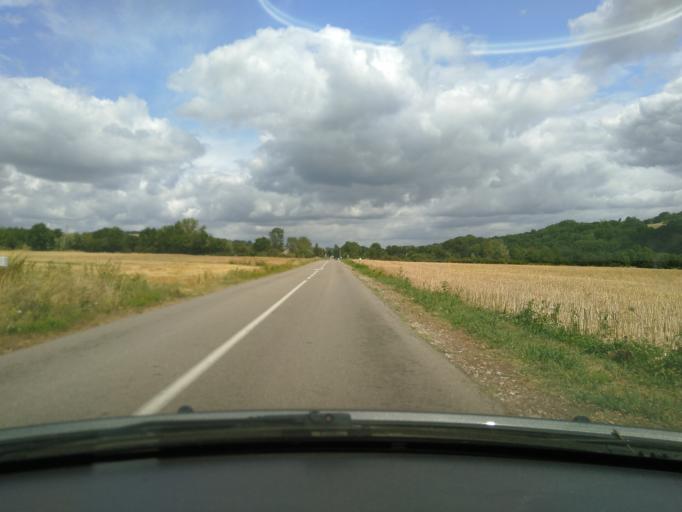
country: FR
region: Rhone-Alpes
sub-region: Departement de l'Isere
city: Beaurepaire
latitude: 45.3871
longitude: 5.0266
